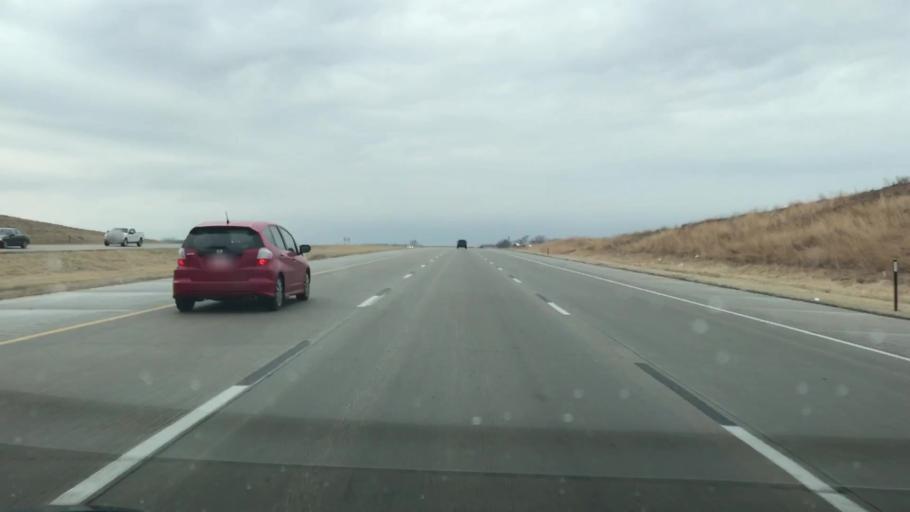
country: US
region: Nebraska
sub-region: Saunders County
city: Ashland
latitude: 40.9988
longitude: -96.3362
